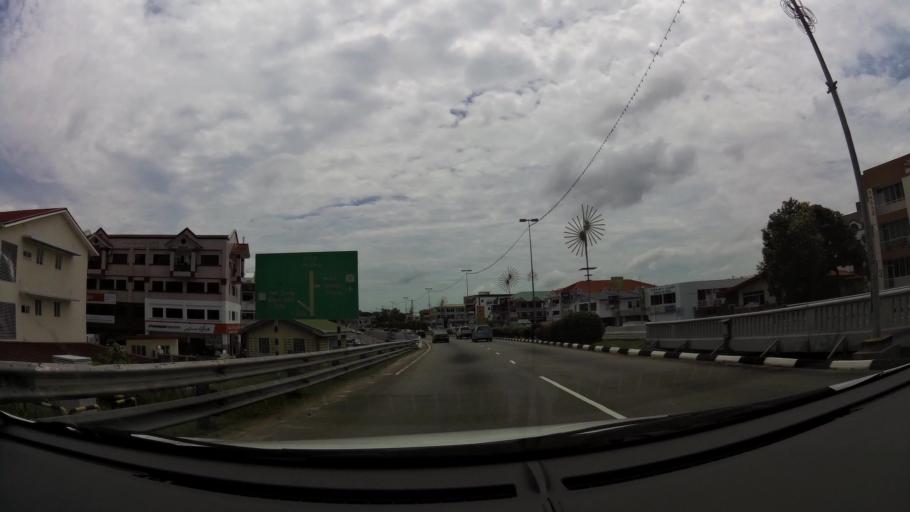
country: BN
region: Brunei and Muara
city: Bandar Seri Begawan
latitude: 4.9086
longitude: 114.9267
